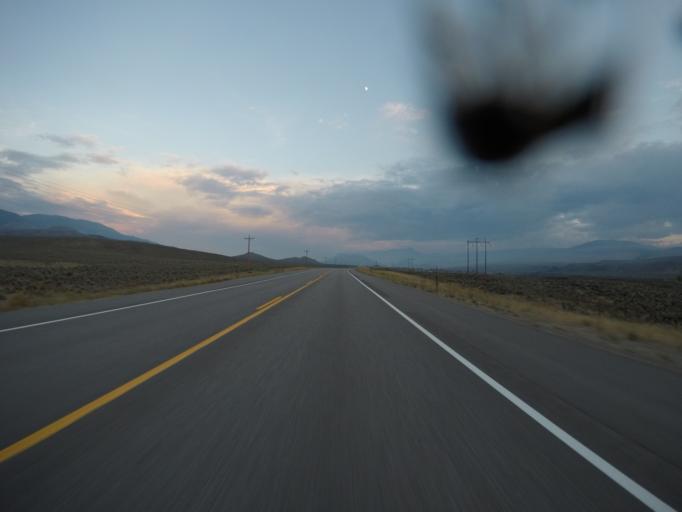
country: US
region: Colorado
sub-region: Grand County
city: Kremmling
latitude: 39.9653
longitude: -106.3499
